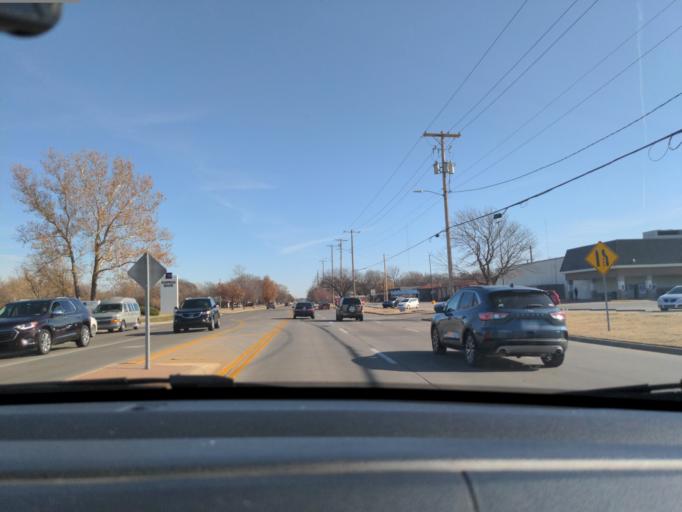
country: US
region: Kansas
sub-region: Sedgwick County
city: Wichita
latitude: 37.6947
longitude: -97.3892
